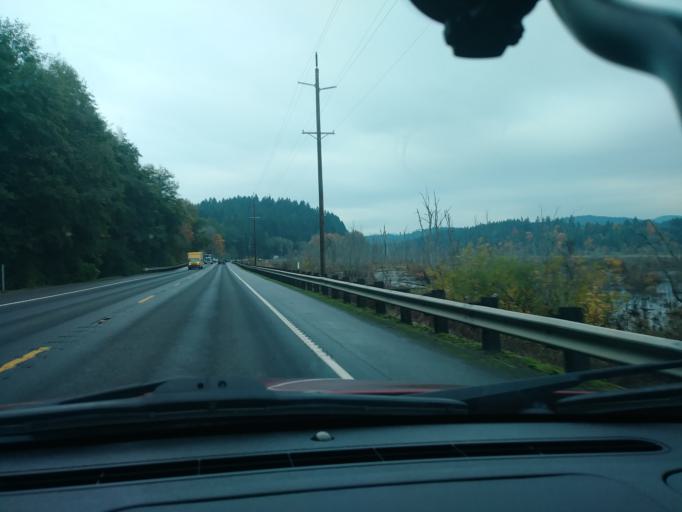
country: US
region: Oregon
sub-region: Washington County
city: Banks
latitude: 45.6113
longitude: -123.1539
